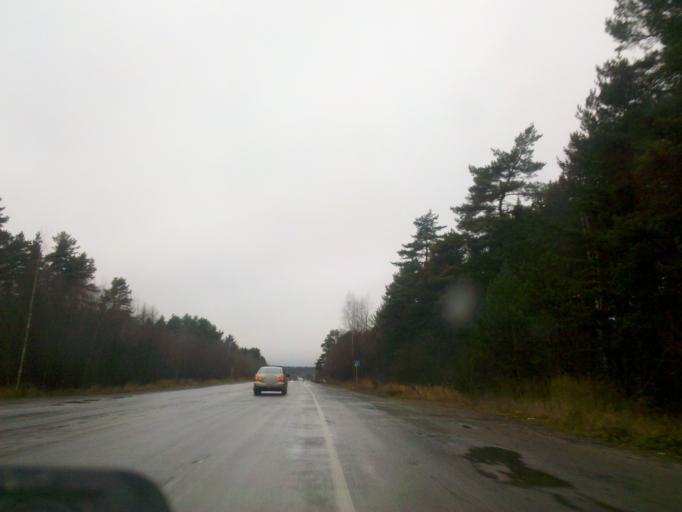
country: RU
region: Republic of Karelia
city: Shuya
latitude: 61.8581
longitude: 34.1738
